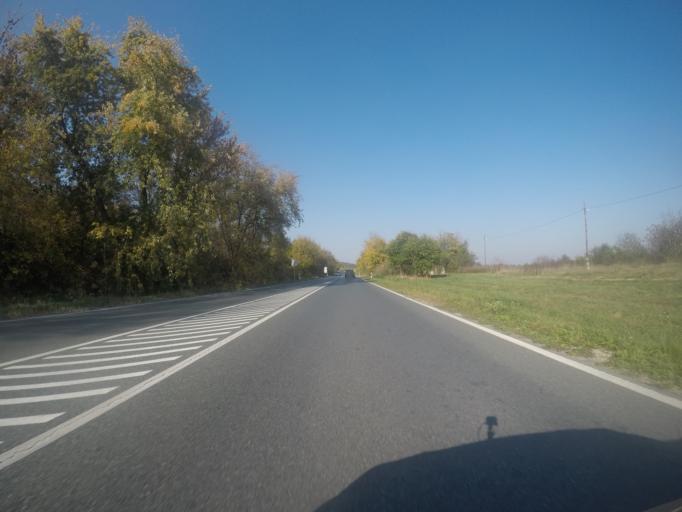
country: HU
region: Tolna
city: Paks
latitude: 46.6678
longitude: 18.8803
